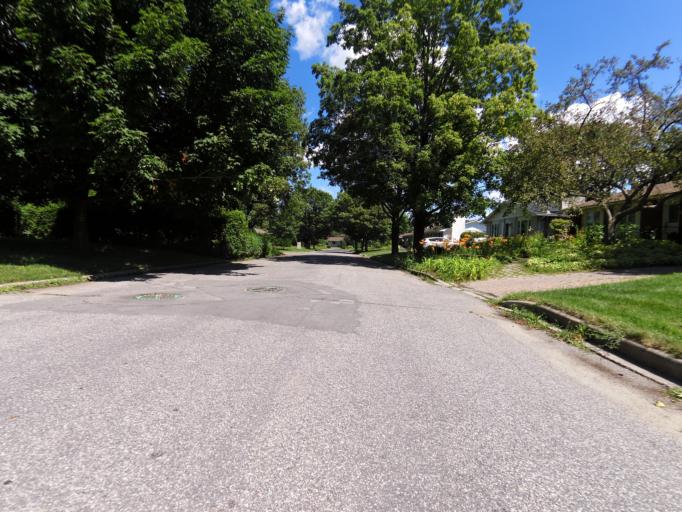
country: CA
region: Ontario
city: Ottawa
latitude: 45.3602
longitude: -75.6843
